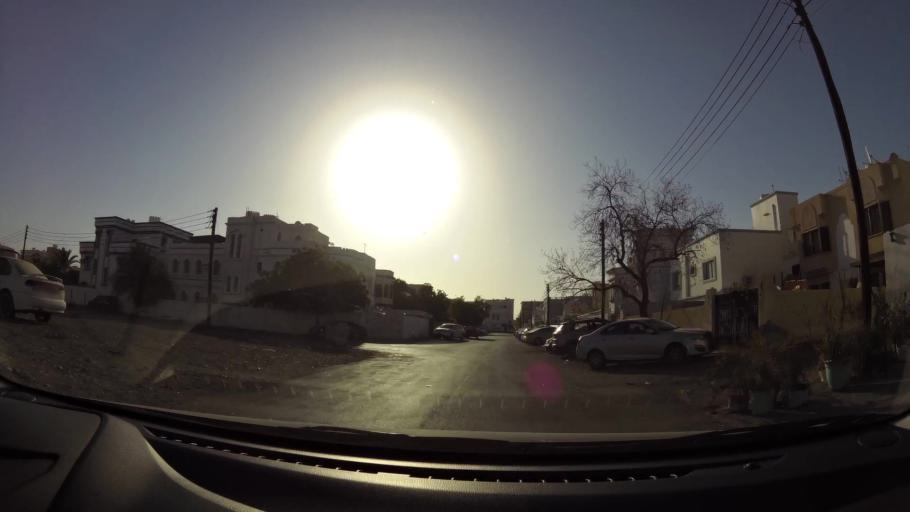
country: OM
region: Muhafazat Masqat
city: As Sib al Jadidah
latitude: 23.6339
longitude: 58.1986
